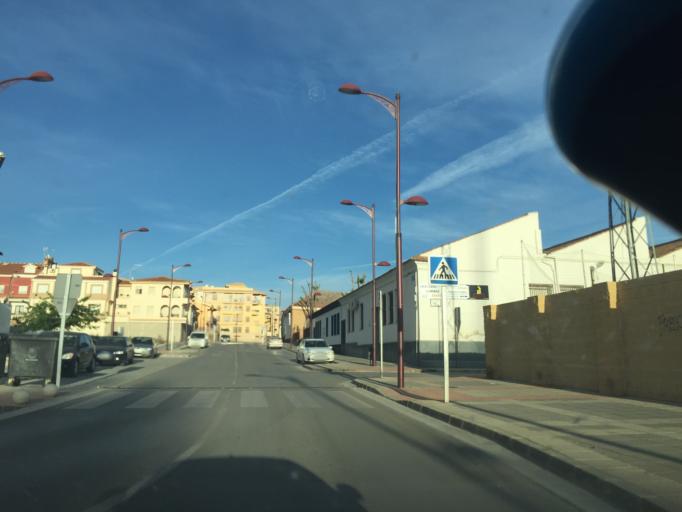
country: ES
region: Andalusia
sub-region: Provincia de Granada
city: Guadix
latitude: 37.3065
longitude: -3.1414
